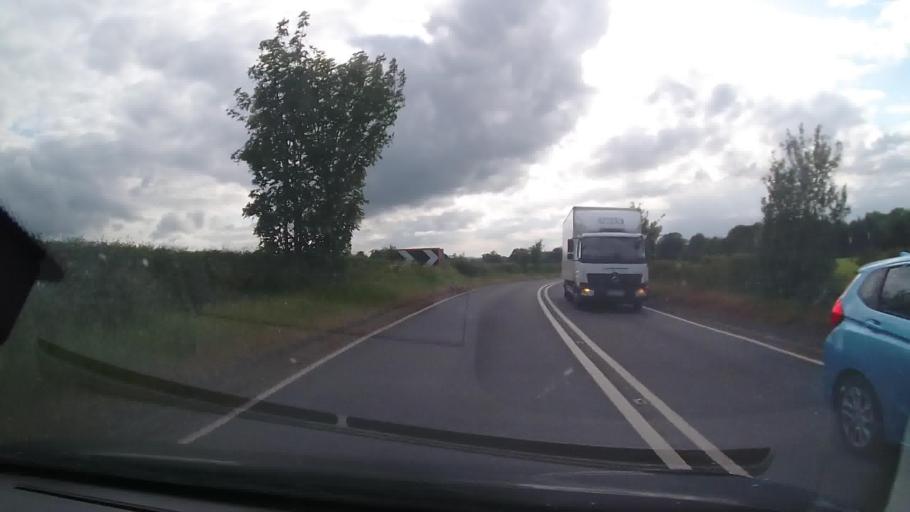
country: GB
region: England
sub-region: Shropshire
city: Berrington
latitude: 52.6814
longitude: -2.6488
